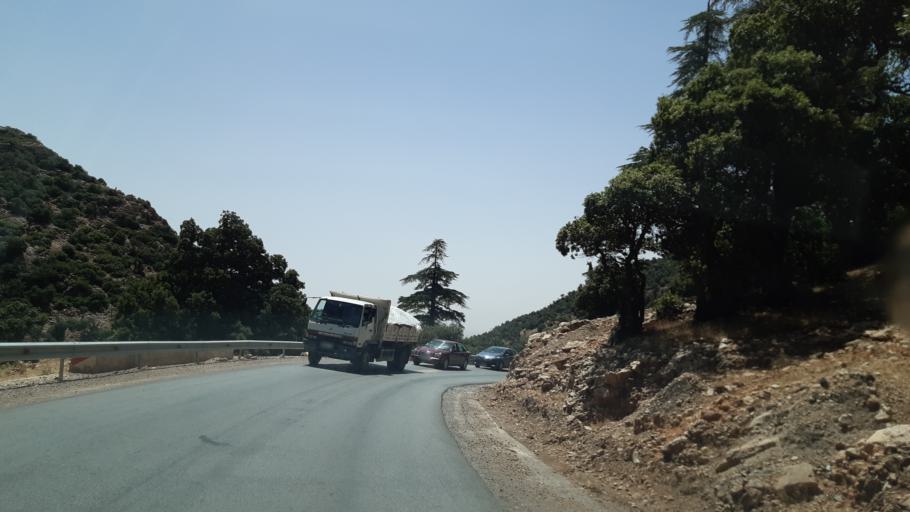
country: MA
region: Meknes-Tafilalet
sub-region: Khenifra
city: Itzer
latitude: 32.9817
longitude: -5.0659
